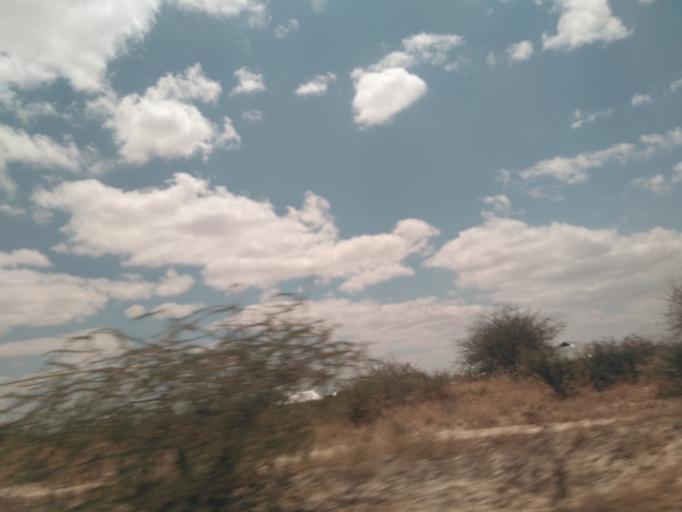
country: TZ
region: Dodoma
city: Kisasa
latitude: -6.1754
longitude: 35.7895
